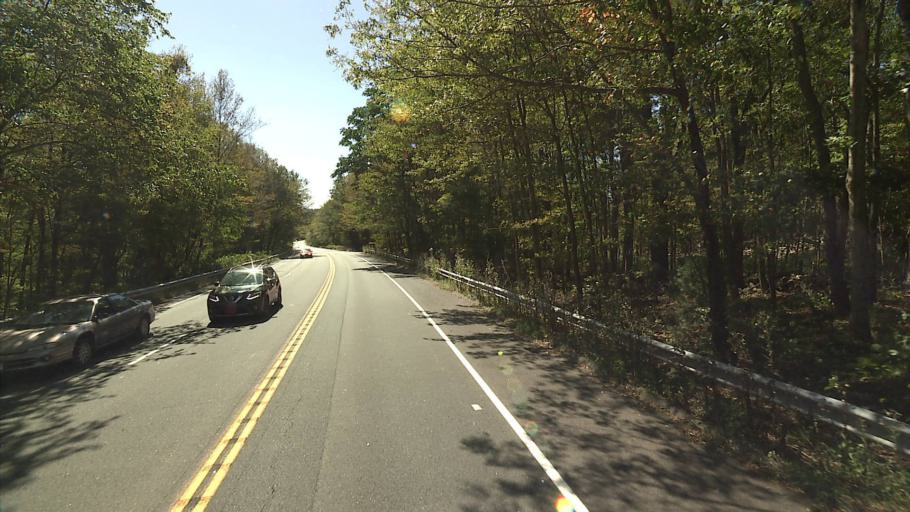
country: US
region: Connecticut
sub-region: New Haven County
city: Woodbridge
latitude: 41.3970
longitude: -72.9742
